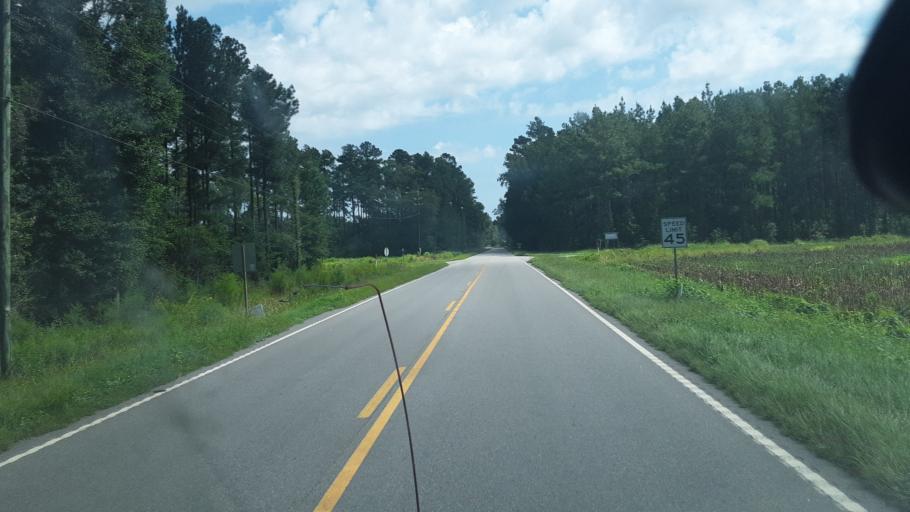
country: US
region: South Carolina
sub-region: Bamberg County
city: Bamberg
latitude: 33.0828
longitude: -81.0188
